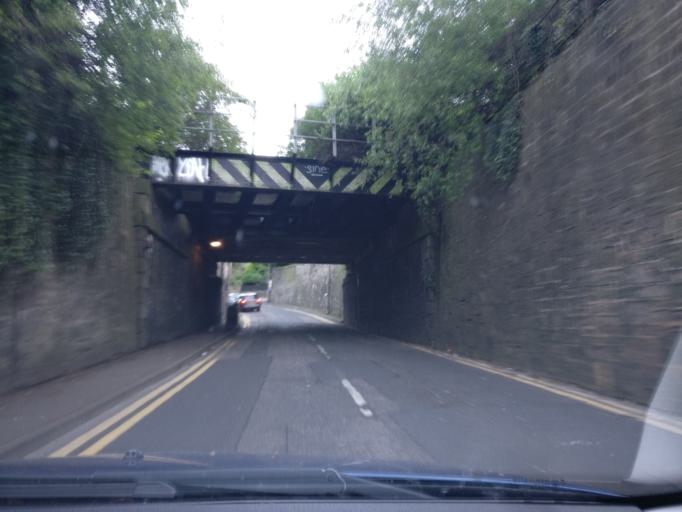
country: GB
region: Scotland
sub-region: West Lothian
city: Seafield
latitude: 55.9566
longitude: -3.1500
